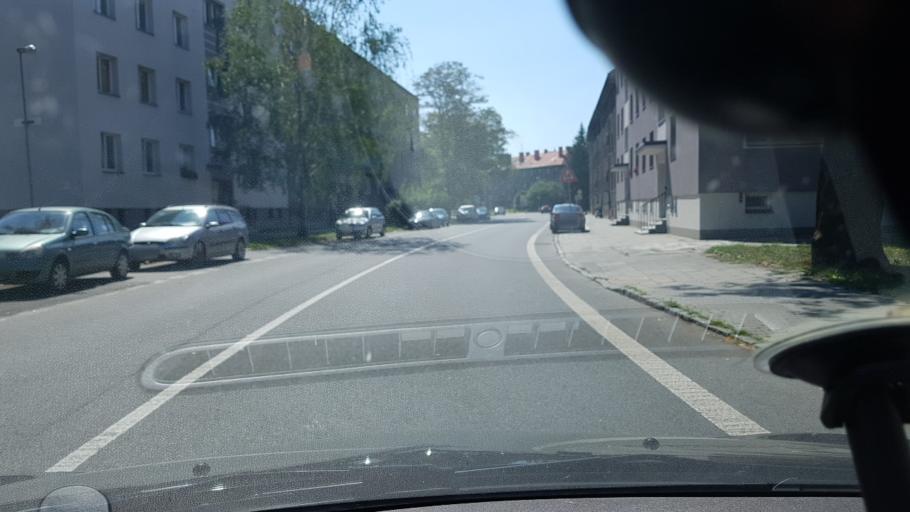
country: CZ
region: Moravskoslezsky
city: Bohumin
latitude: 49.9044
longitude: 18.3515
